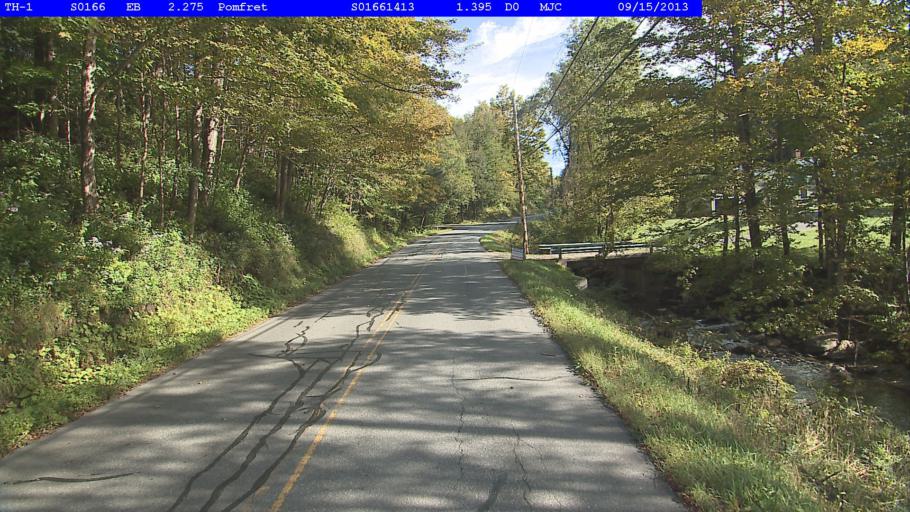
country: US
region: Vermont
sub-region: Windsor County
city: Woodstock
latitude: 43.6681
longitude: -72.5377
